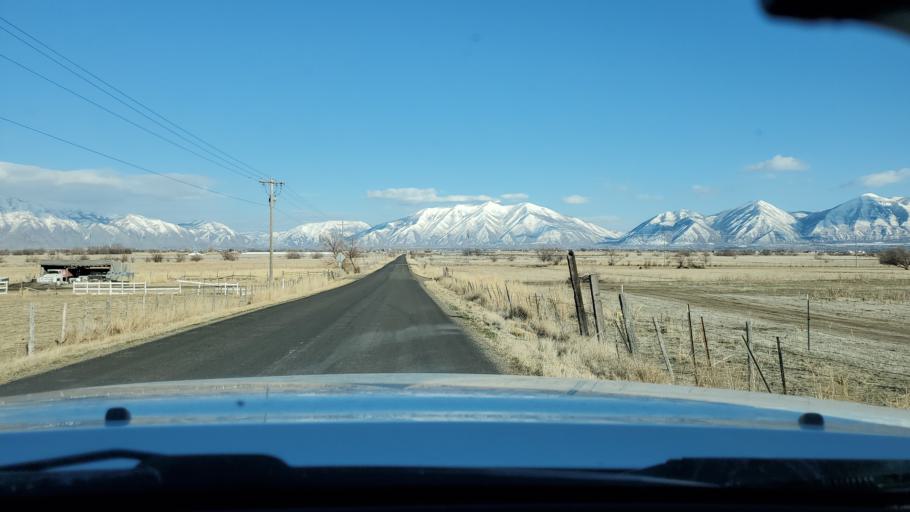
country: US
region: Utah
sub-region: Utah County
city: West Mountain
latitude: 40.1140
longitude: -111.8002
